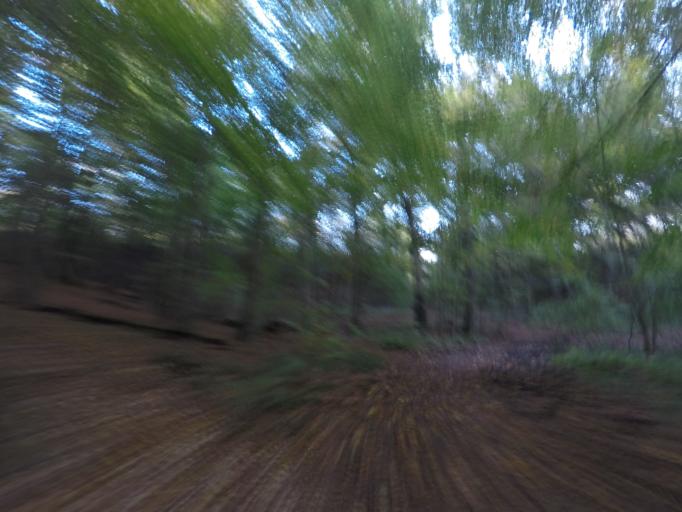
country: LU
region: Luxembourg
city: Itzig
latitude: 49.5891
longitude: 6.1610
